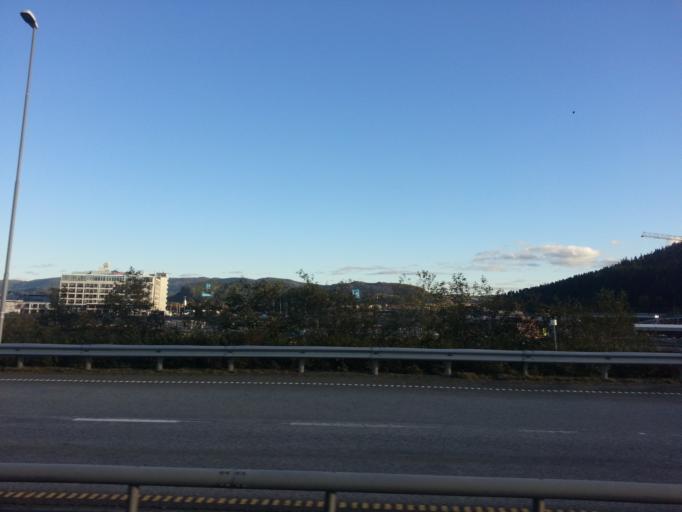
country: NO
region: Nord-Trondelag
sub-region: Stjordal
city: Stjordal
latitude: 63.4499
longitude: 10.9060
